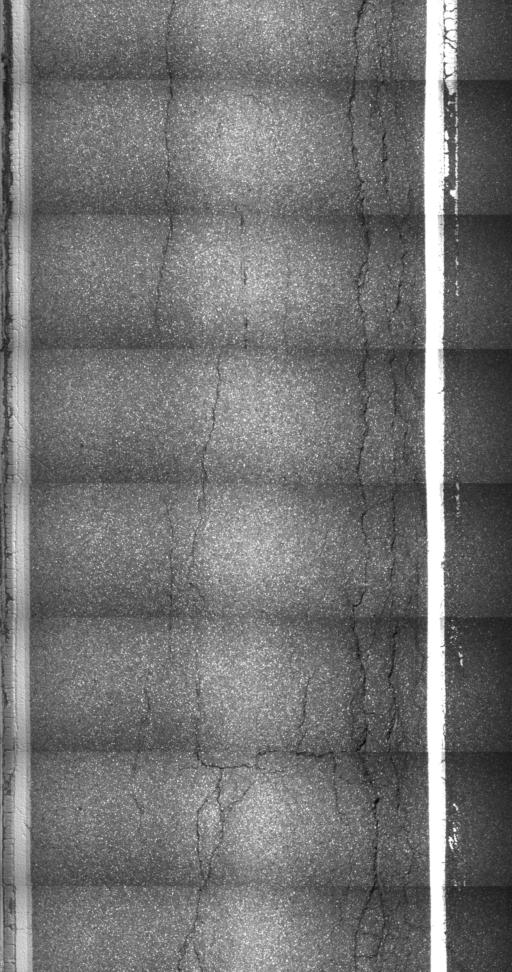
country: US
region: Vermont
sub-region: Chittenden County
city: Williston
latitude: 44.4339
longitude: -73.0209
